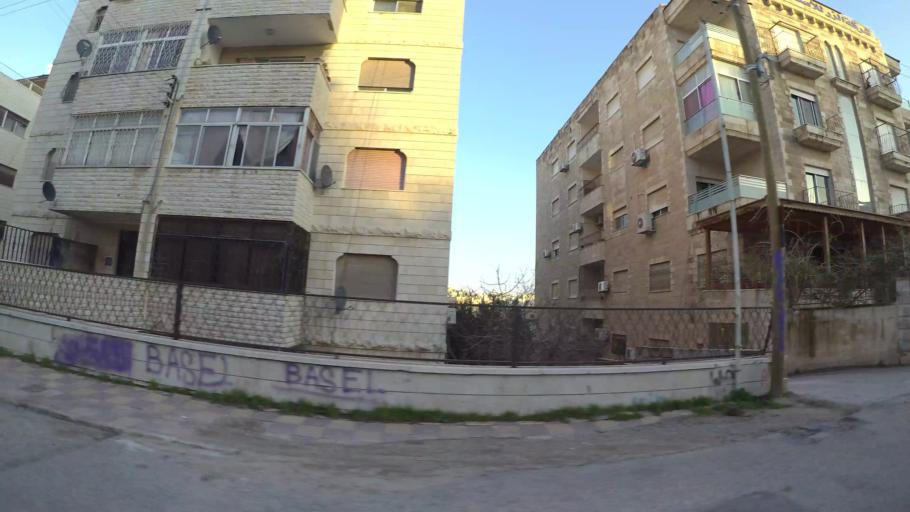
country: JO
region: Amman
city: Al Jubayhah
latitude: 31.9893
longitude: 35.8773
